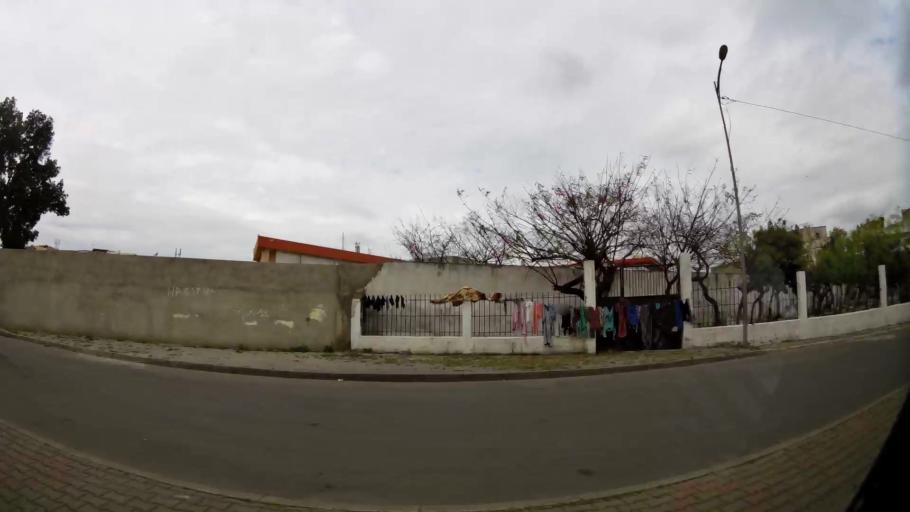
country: MA
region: Grand Casablanca
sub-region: Casablanca
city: Casablanca
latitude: 33.5800
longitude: -7.5632
